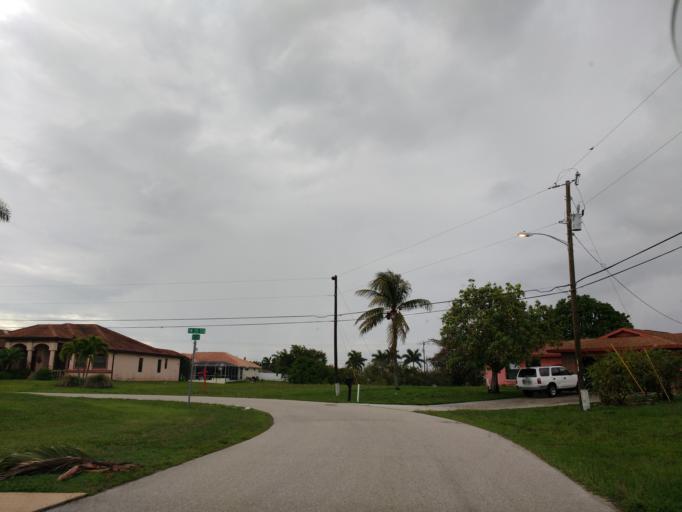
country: US
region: Florida
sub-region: Lee County
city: Cape Coral
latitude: 26.6009
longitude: -82.0241
